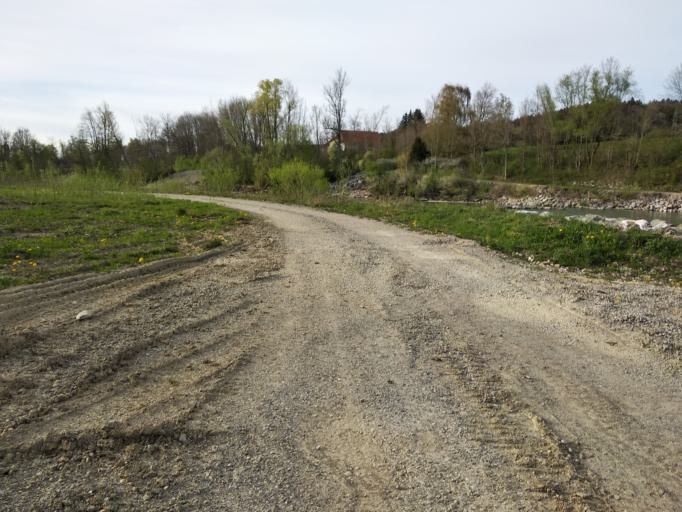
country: DE
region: Bavaria
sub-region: Swabia
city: Kronburg
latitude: 47.8952
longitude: 10.1399
